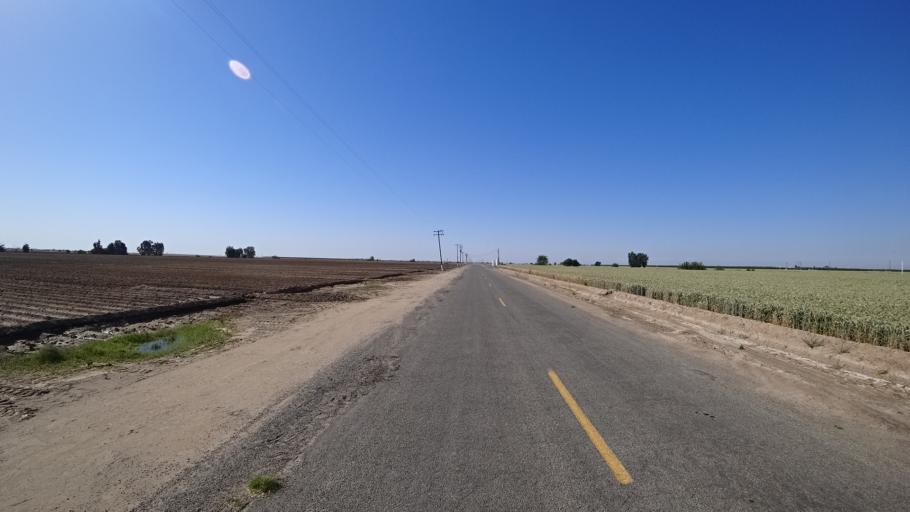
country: US
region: California
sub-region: Kings County
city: Home Garden
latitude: 36.2220
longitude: -119.5651
